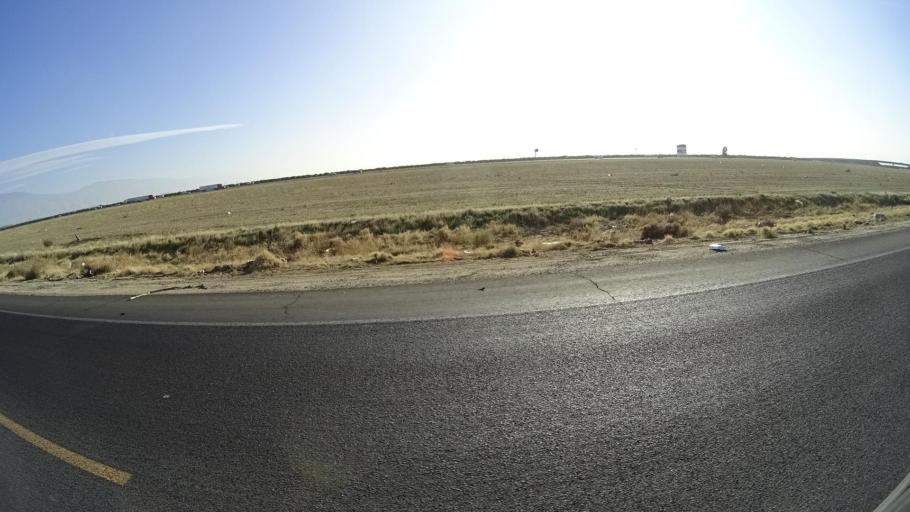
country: US
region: California
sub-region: Kern County
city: Lamont
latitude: 35.3353
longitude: -118.8186
